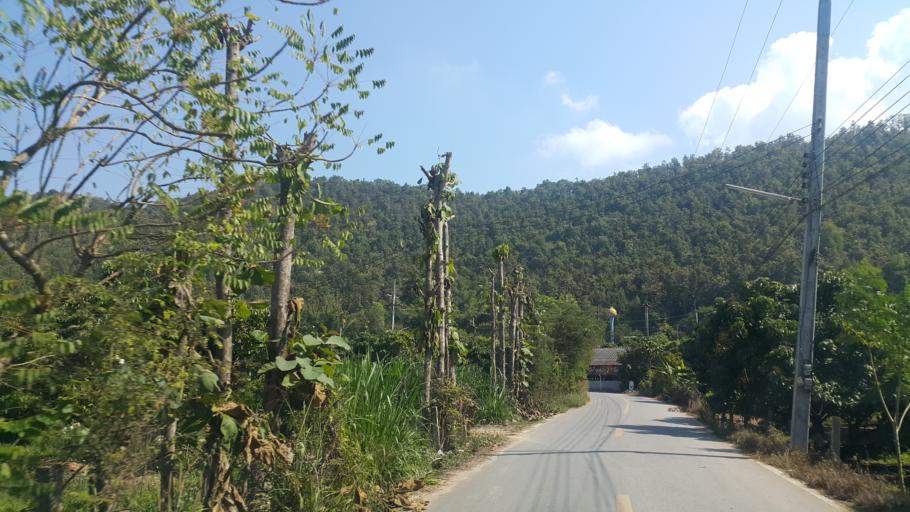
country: TH
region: Chiang Mai
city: San Kamphaeng
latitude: 18.6946
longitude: 99.1683
